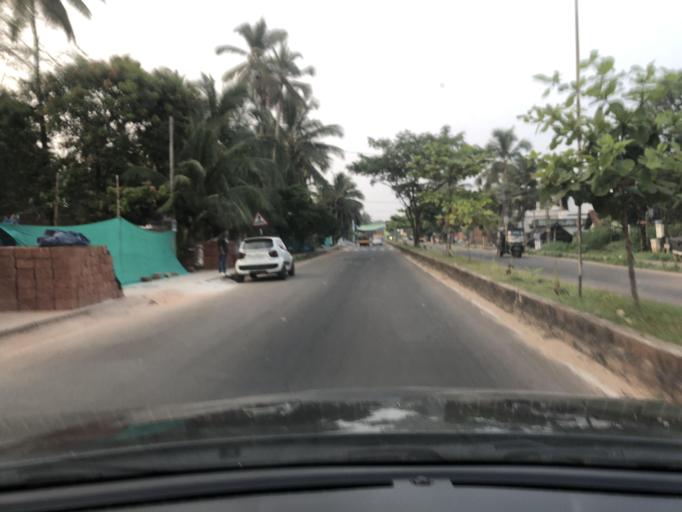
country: IN
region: Kerala
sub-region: Kozhikode
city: Kozhikode
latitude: 11.2996
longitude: 75.7556
